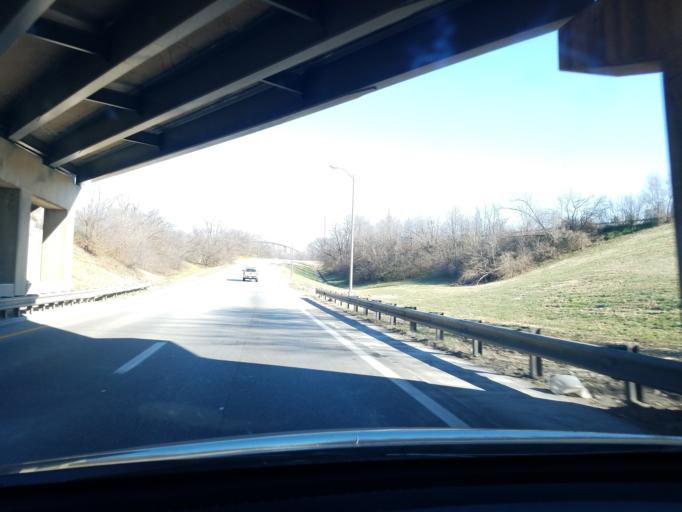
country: US
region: Indiana
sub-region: Floyd County
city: New Albany
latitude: 38.2759
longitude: -85.8092
